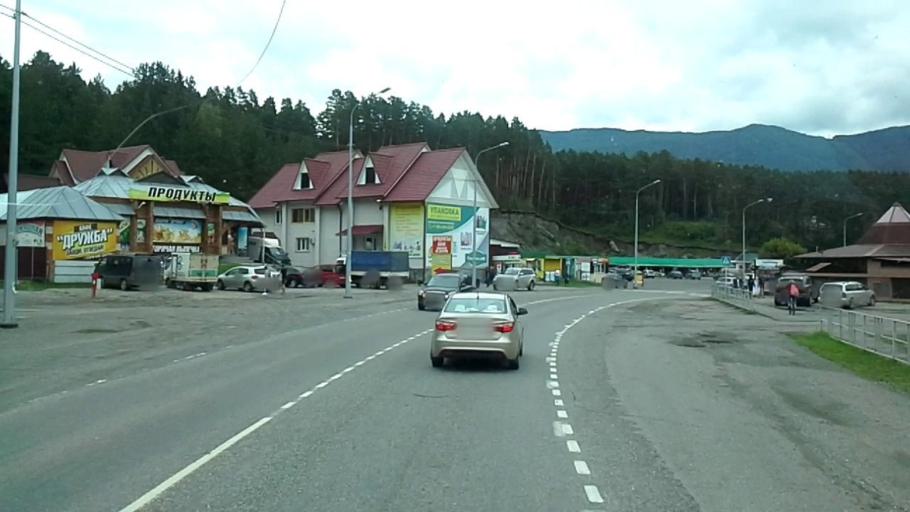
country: RU
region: Altay
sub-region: Mayminskiy Rayon
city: Manzherok
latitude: 51.8336
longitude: 85.7801
